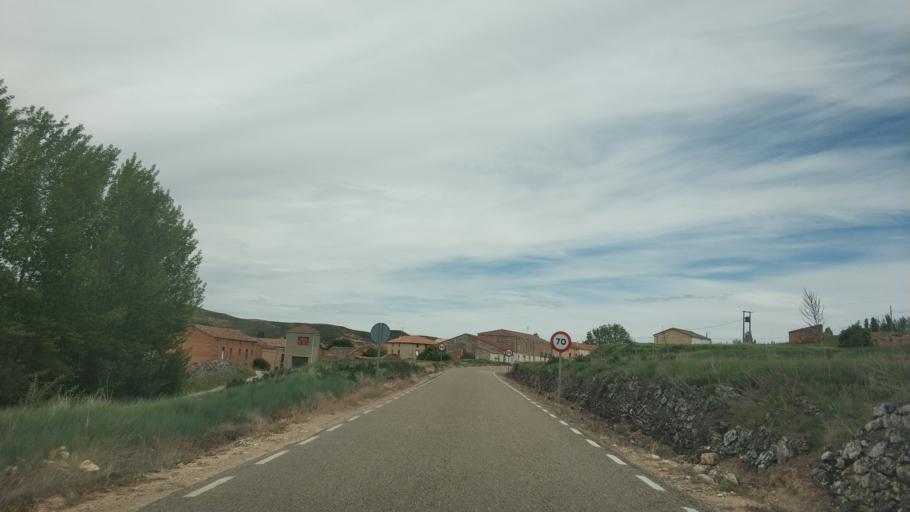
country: ES
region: Castille and Leon
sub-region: Provincia de Soria
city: Berlanga de Duero
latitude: 41.4422
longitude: -2.8231
